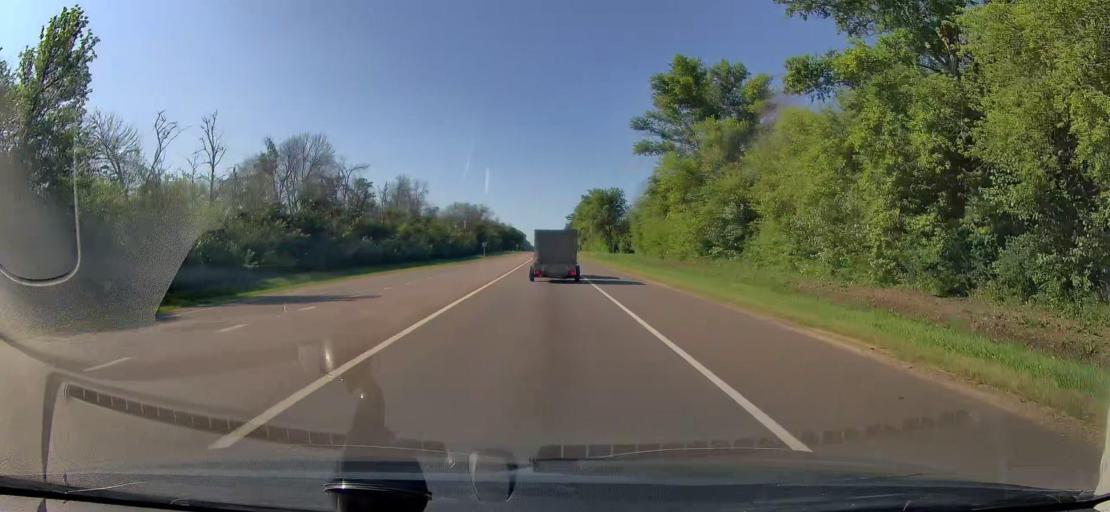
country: RU
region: Orjol
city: Kromy
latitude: 52.6067
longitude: 35.7618
